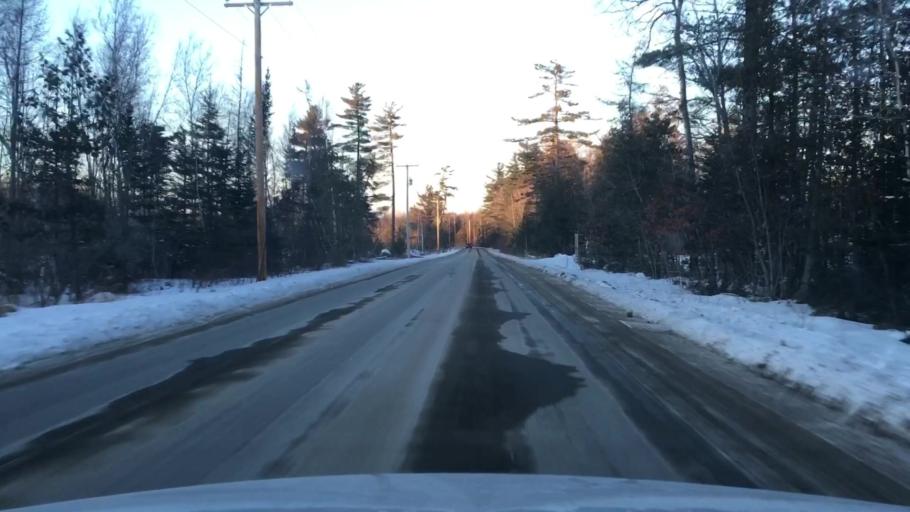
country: US
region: Maine
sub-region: Penobscot County
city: Orrington
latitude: 44.7097
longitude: -68.7539
